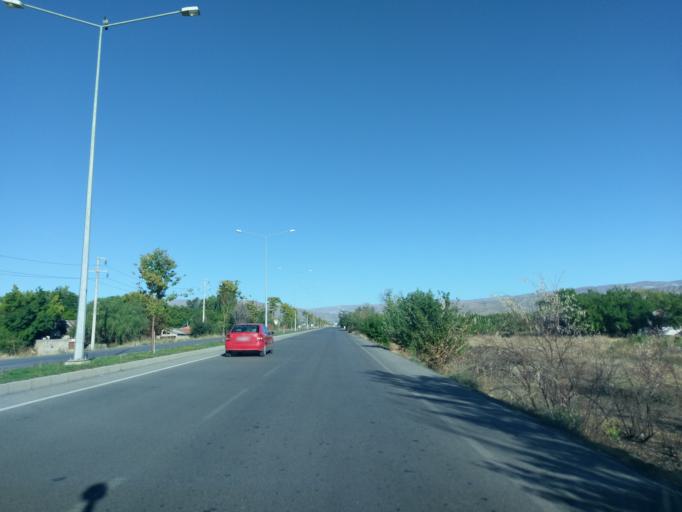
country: TR
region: Erzincan
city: Erzincan
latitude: 39.7739
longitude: 39.4203
